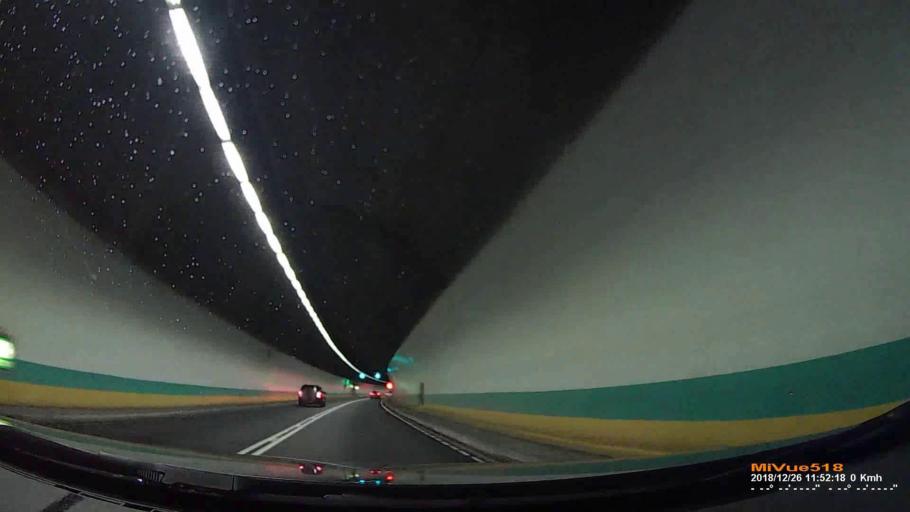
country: TW
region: Taiwan
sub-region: Keelung
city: Keelung
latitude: 24.9678
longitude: 121.6837
